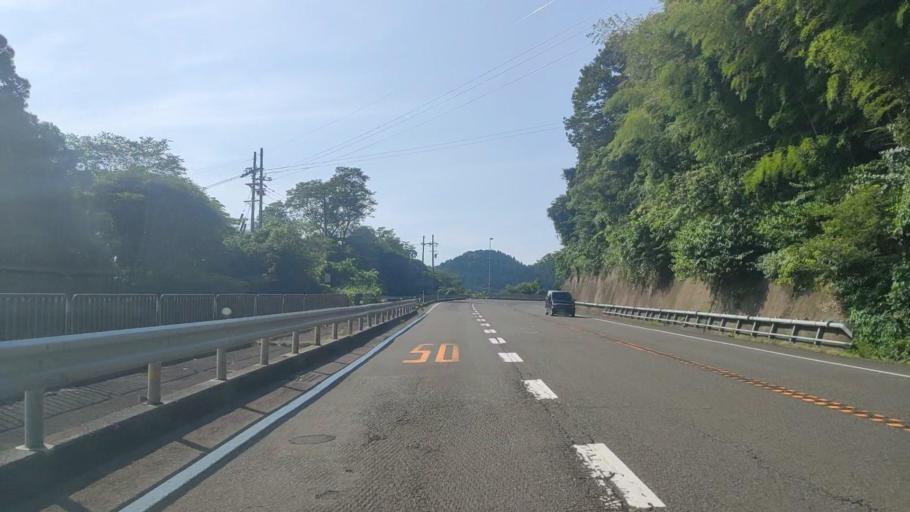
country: JP
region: Fukui
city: Tsuruga
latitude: 35.7573
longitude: 136.1059
